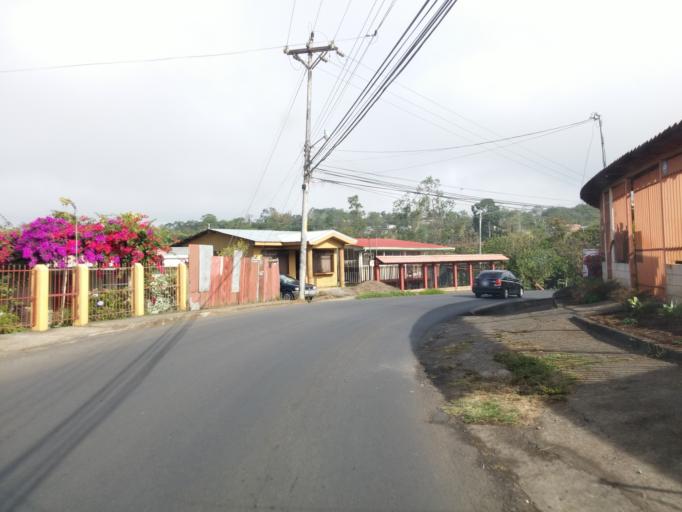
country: CR
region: Alajuela
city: San Ramon
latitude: 10.1091
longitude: -84.4683
